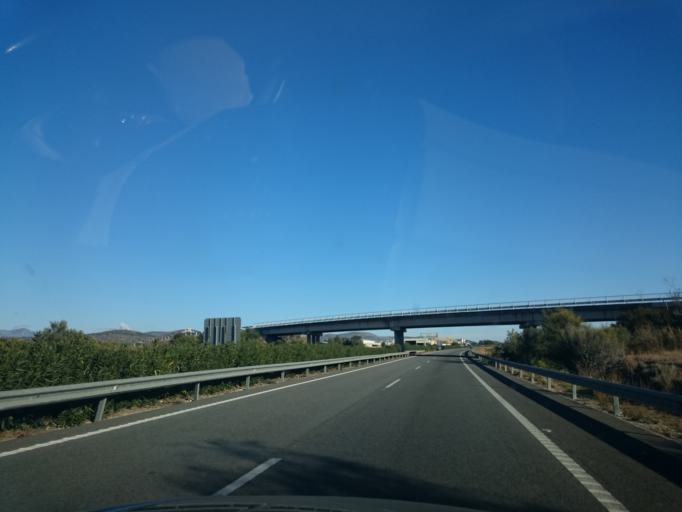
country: ES
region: Catalonia
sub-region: Provincia de Tarragona
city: Ulldecona
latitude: 40.5656
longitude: 0.4310
